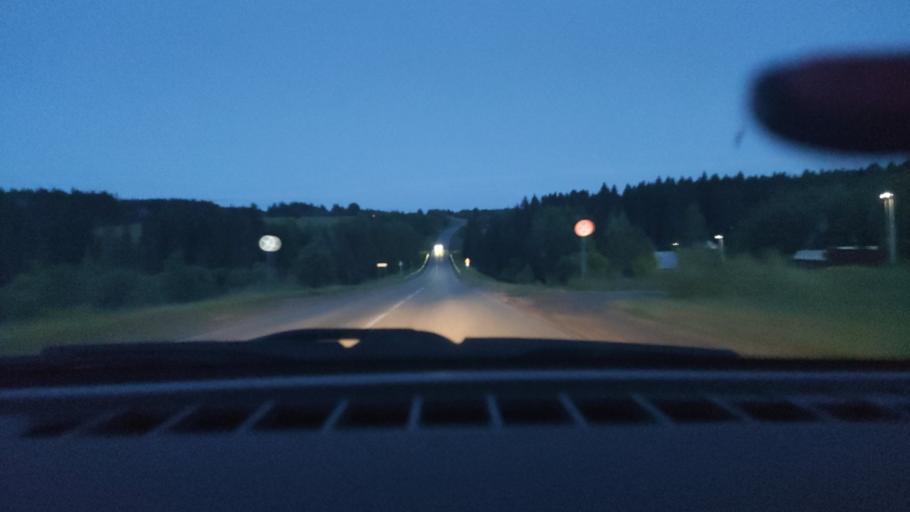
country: RU
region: Perm
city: Polazna
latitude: 58.2813
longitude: 56.4124
